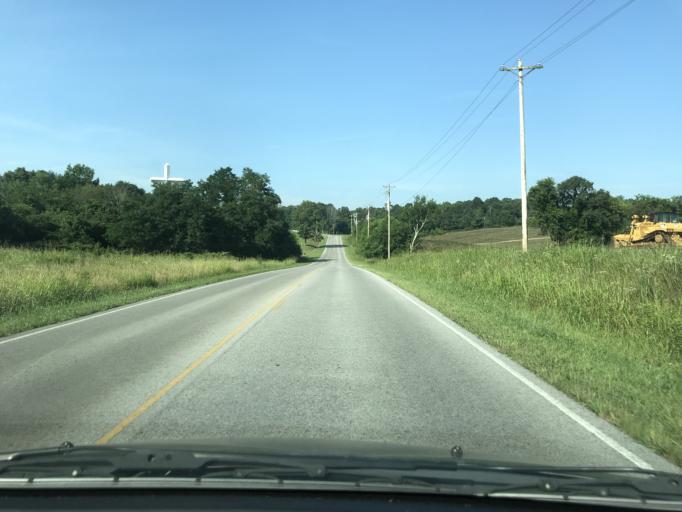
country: US
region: Tennessee
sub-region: Loudon County
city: Loudon
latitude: 35.7806
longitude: -84.3491
